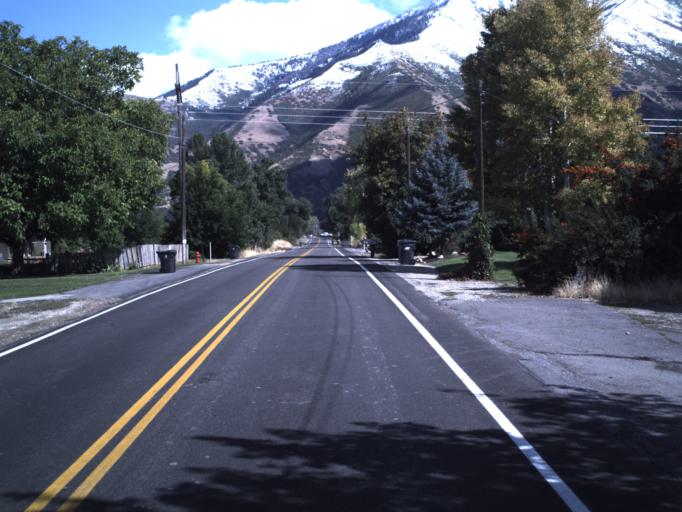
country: US
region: Utah
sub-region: Utah County
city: Mapleton
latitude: 40.1158
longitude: -111.5836
